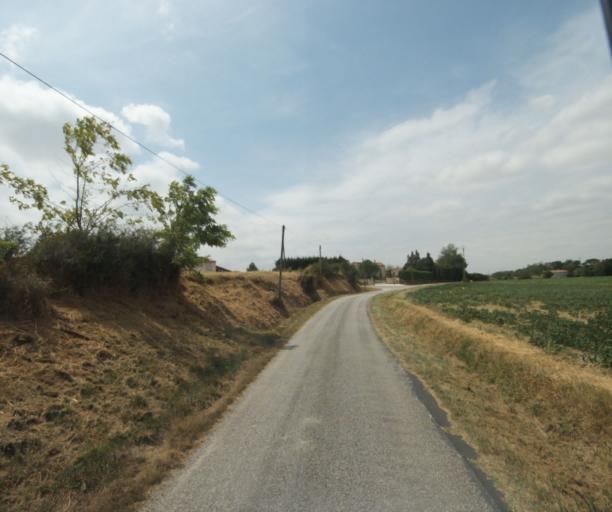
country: FR
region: Midi-Pyrenees
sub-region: Departement de la Haute-Garonne
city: Revel
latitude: 43.4352
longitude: 1.9619
